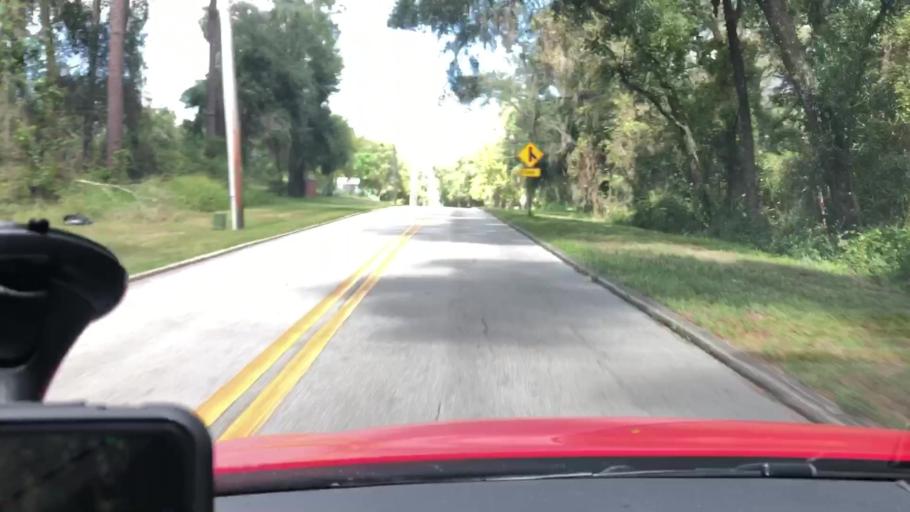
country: US
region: Florida
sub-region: Volusia County
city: North DeLand
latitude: 29.0479
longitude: -81.3165
